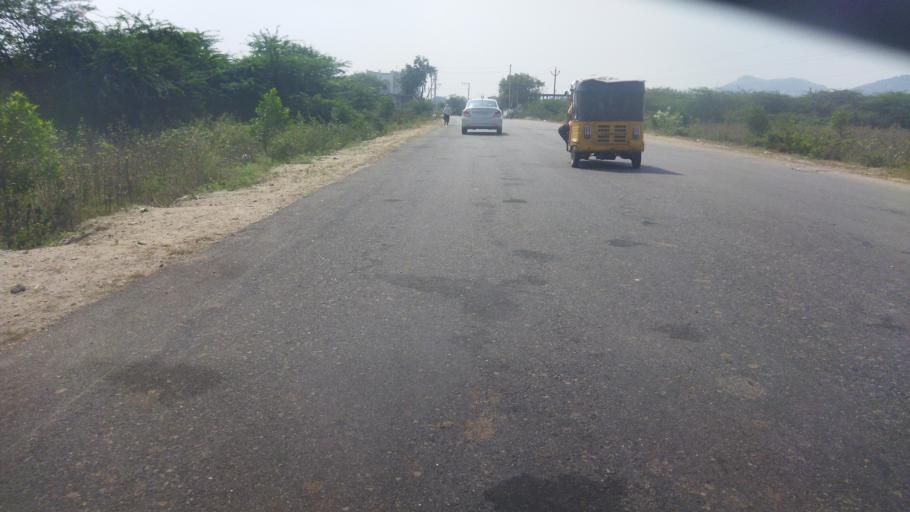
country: IN
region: Telangana
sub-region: Nalgonda
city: Nalgonda
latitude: 17.0807
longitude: 79.2838
